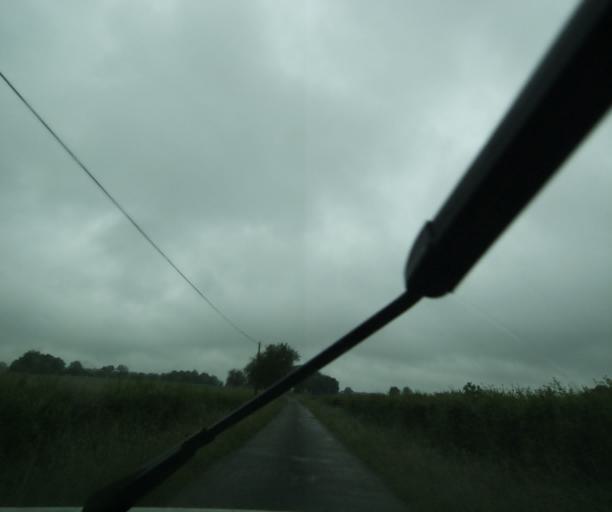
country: FR
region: Bourgogne
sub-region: Departement de Saone-et-Loire
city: Ciry-le-Noble
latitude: 46.5621
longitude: 4.3221
